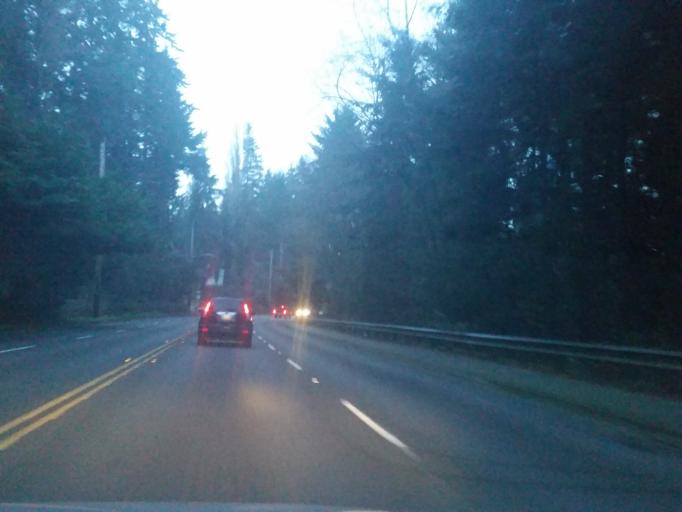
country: US
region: Washington
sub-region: Snohomish County
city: Mountlake Terrace
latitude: 47.7638
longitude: -122.3134
